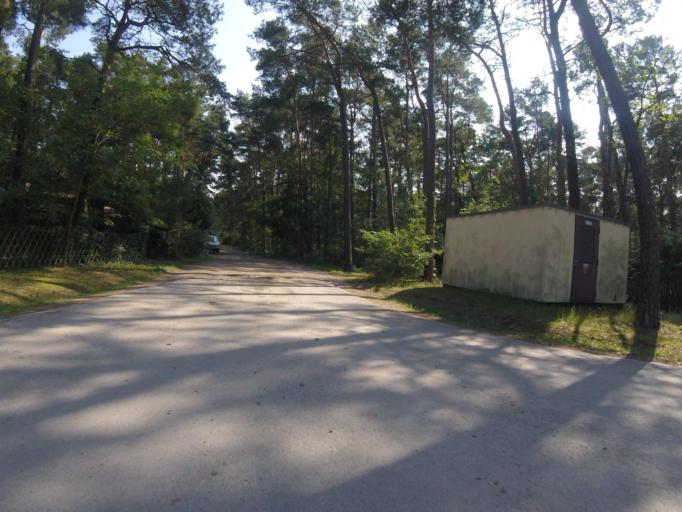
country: DE
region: Brandenburg
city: Bestensee
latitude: 52.2603
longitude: 13.7451
